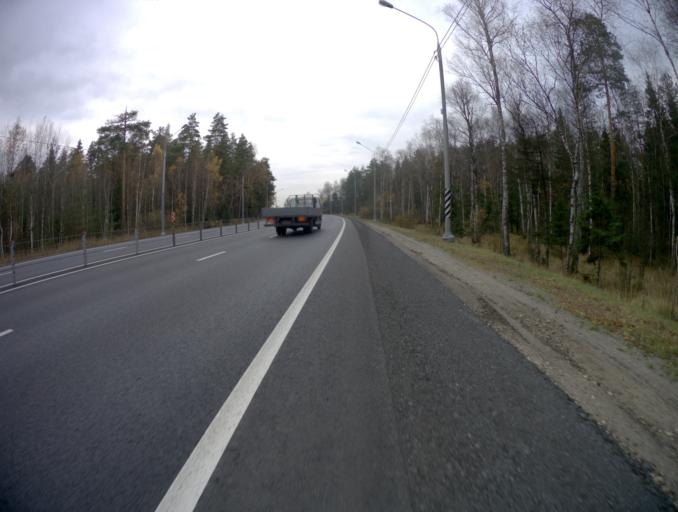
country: RU
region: Moskovskaya
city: Malaya Dubna
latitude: 55.8675
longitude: 38.9641
